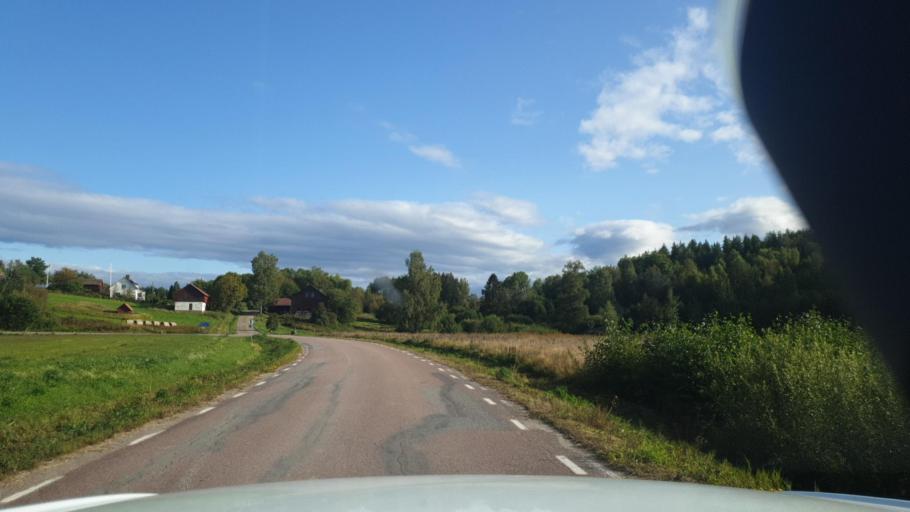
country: SE
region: Vaermland
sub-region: Eda Kommun
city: Amotfors
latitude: 59.8302
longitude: 12.3581
